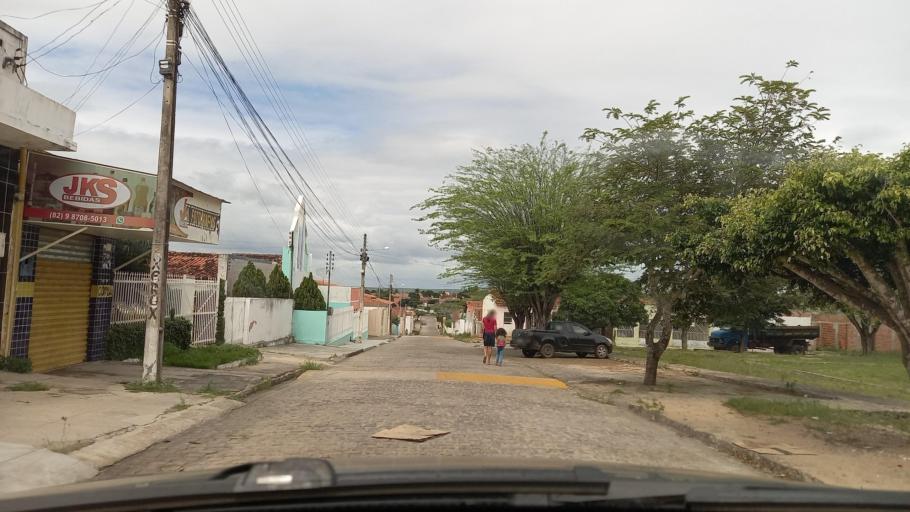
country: BR
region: Sergipe
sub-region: Caninde De Sao Francisco
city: Caninde de Sao Francisco
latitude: -9.6056
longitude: -37.7608
